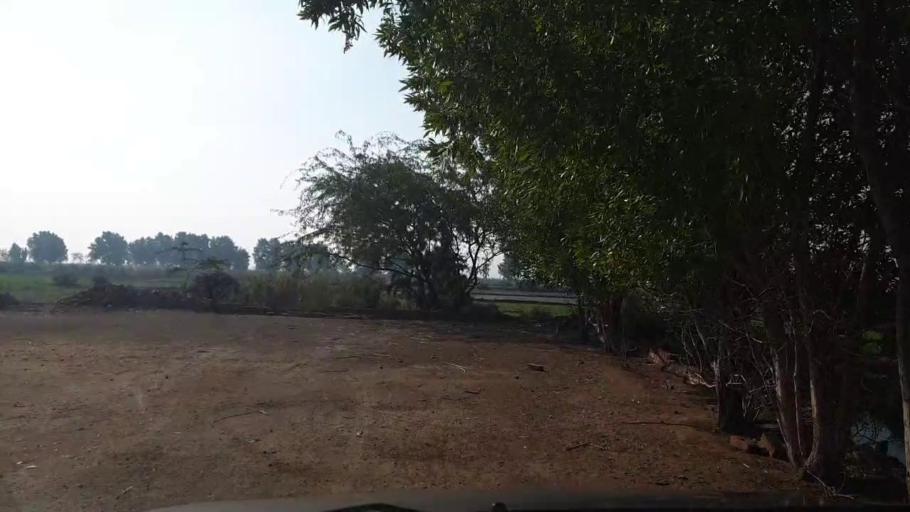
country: PK
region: Sindh
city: Sinjhoro
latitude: 26.0343
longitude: 68.7901
